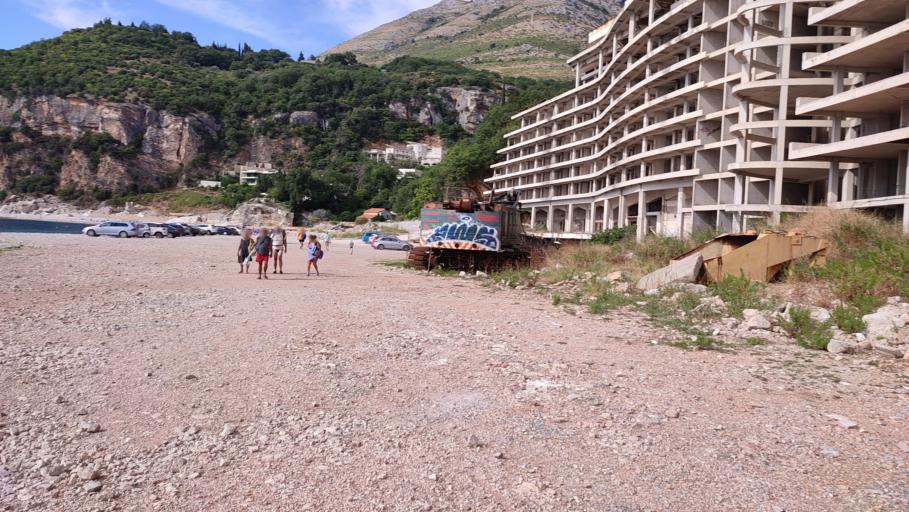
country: ME
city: Petrovac na Moru
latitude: 42.2099
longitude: 18.9261
